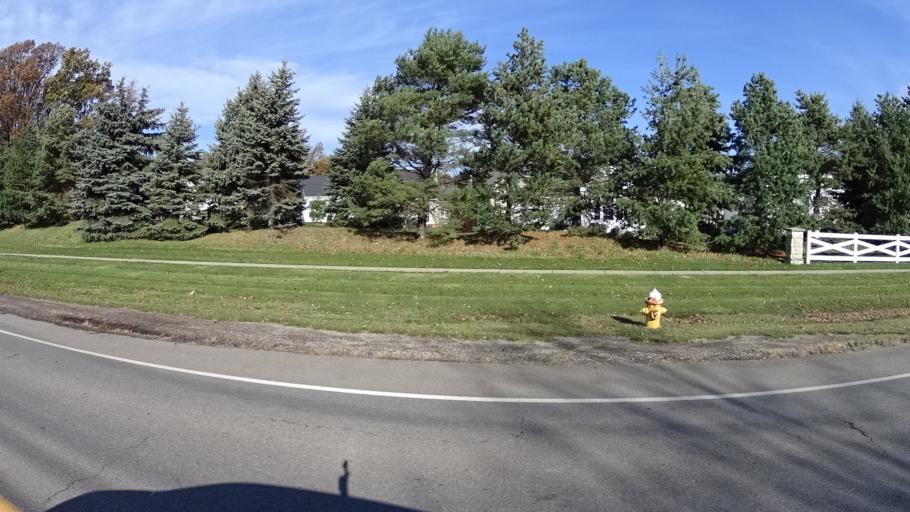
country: US
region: Ohio
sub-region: Lorain County
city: Avon Lake
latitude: 41.4933
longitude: -82.0407
